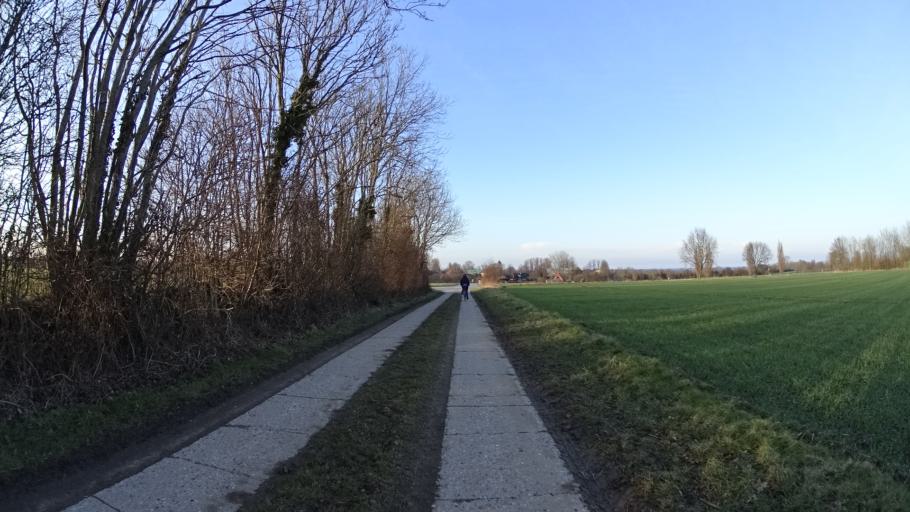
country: DE
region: Schleswig-Holstein
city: Stakendorf
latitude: 54.3830
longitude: 10.4277
